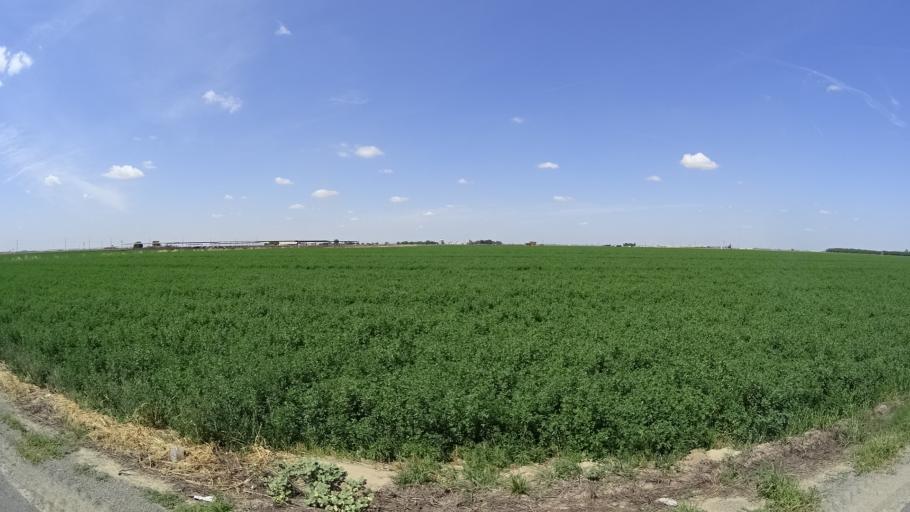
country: US
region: California
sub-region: Tulare County
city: Goshen
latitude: 36.3025
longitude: -119.4747
